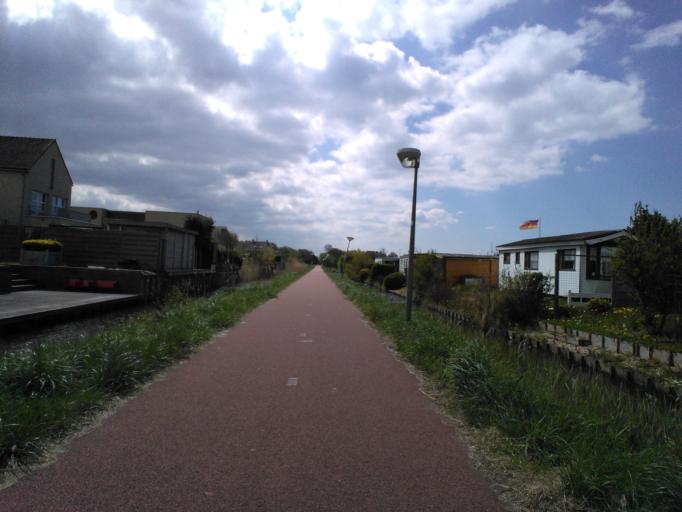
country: NL
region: South Holland
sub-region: Gemeente Rotterdam
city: Hoek van Holland
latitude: 51.9927
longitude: 4.1325
